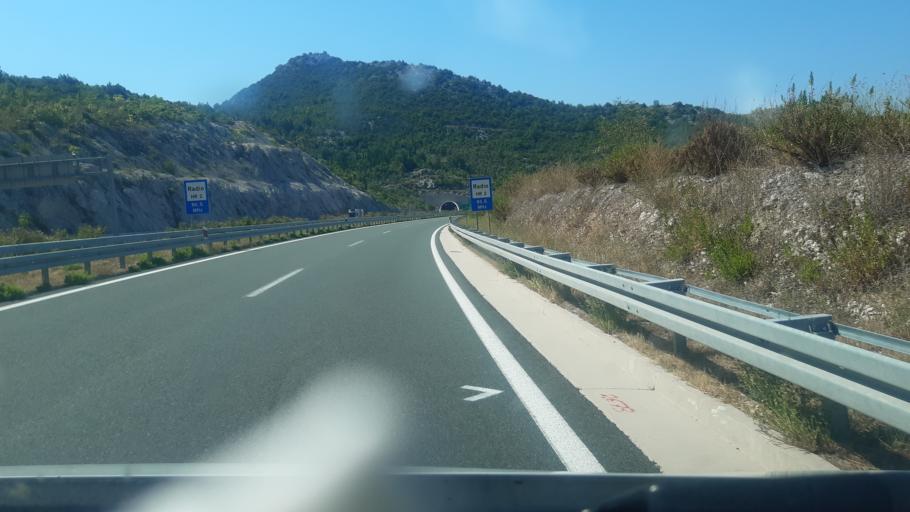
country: BA
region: Federation of Bosnia and Herzegovina
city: Ljubuski
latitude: 43.1319
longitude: 17.4845
